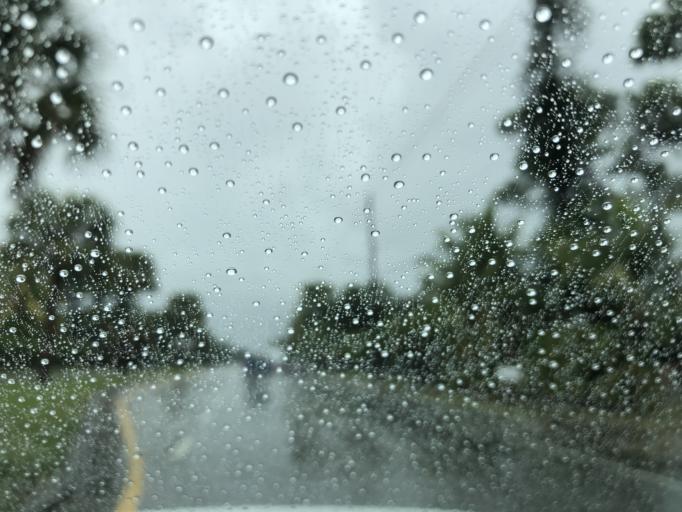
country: US
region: Florida
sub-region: Palm Beach County
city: Haverhill
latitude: 26.6932
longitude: -80.1197
